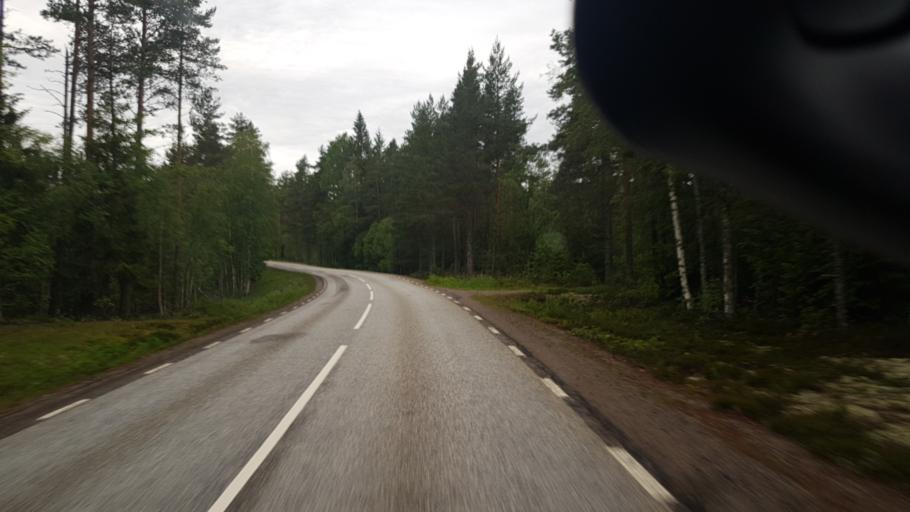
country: SE
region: Vaermland
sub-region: Arjangs Kommun
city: Arjaeng
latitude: 59.5650
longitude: 12.1913
